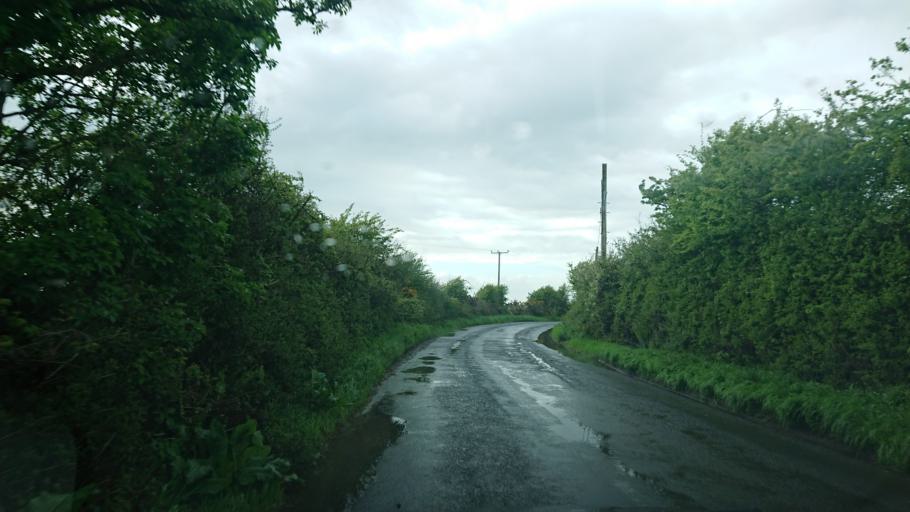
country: IE
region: Munster
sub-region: Waterford
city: Waterford
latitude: 52.2203
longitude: -7.0724
